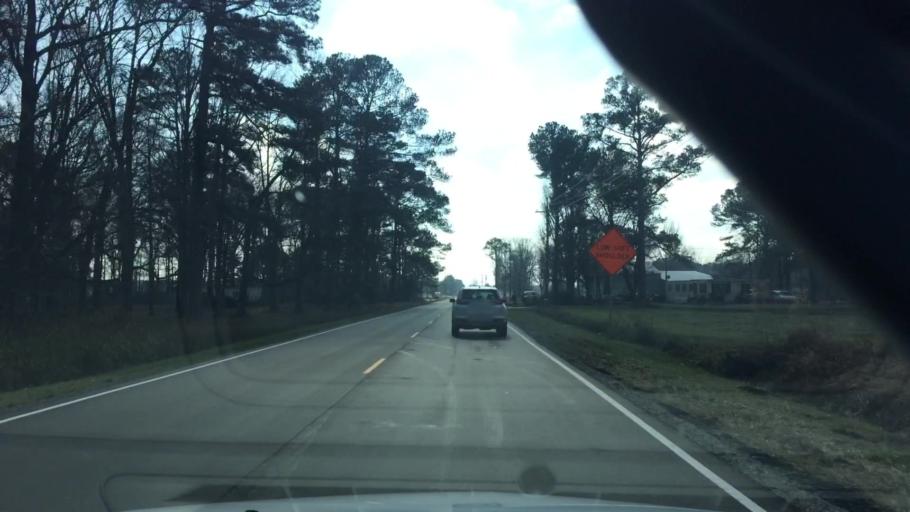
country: US
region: North Carolina
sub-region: Duplin County
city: Beulaville
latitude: 34.9627
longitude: -77.7641
